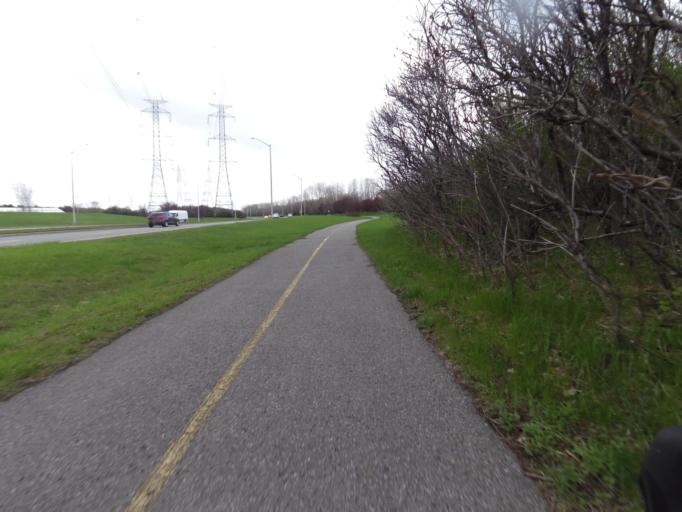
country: CA
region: Ontario
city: Bells Corners
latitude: 45.3265
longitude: -75.7566
